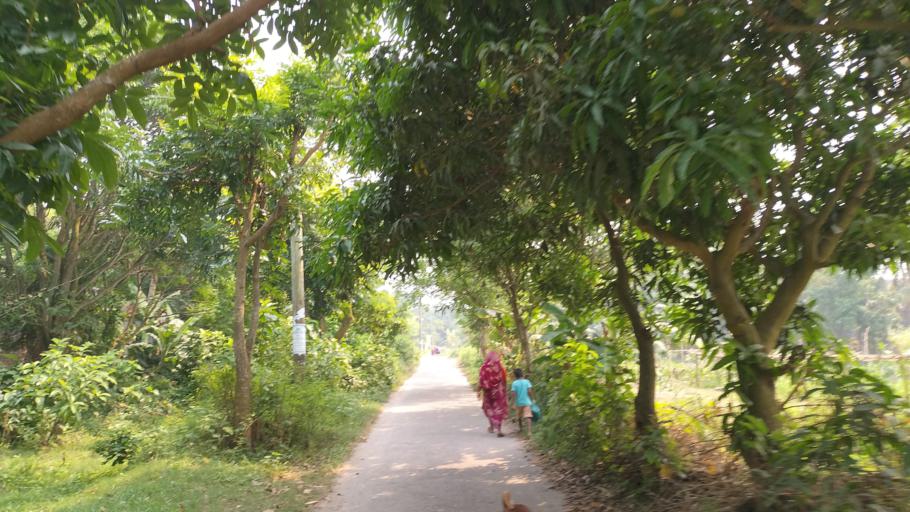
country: BD
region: Dhaka
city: Azimpur
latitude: 23.6923
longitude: 90.2994
